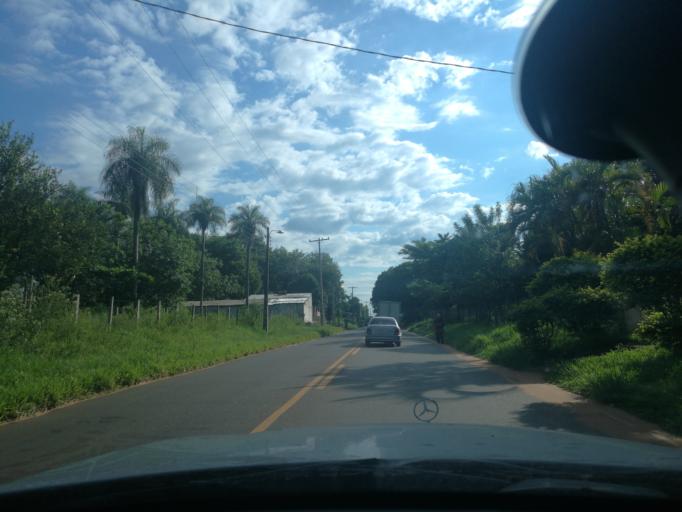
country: PY
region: Central
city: San Lorenzo
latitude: -25.3091
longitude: -57.4683
